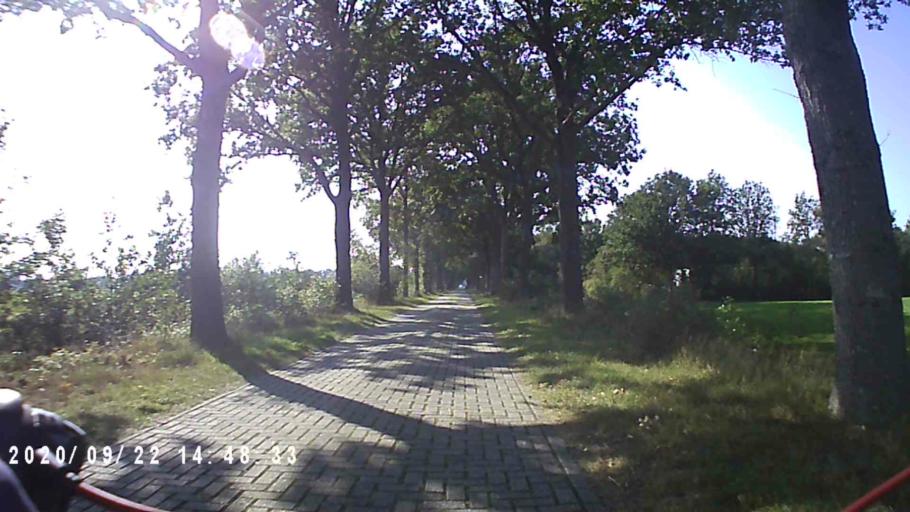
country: NL
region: Groningen
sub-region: Gemeente Leek
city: Leek
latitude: 53.0102
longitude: 6.3449
